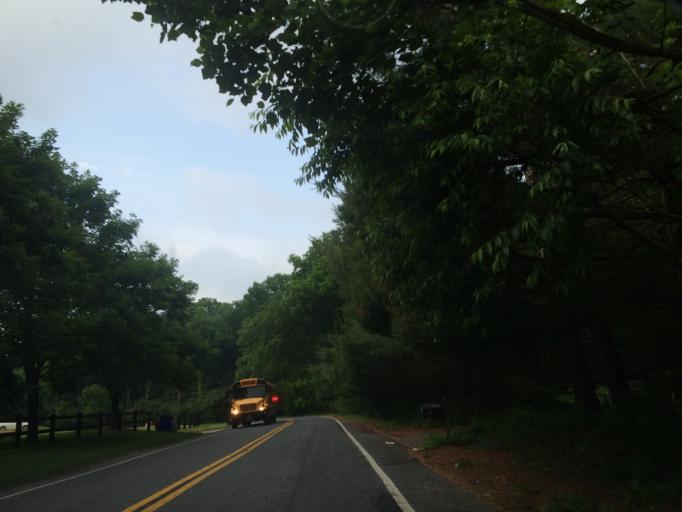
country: US
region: Maryland
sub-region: Carroll County
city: Sykesville
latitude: 39.3257
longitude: -77.0534
